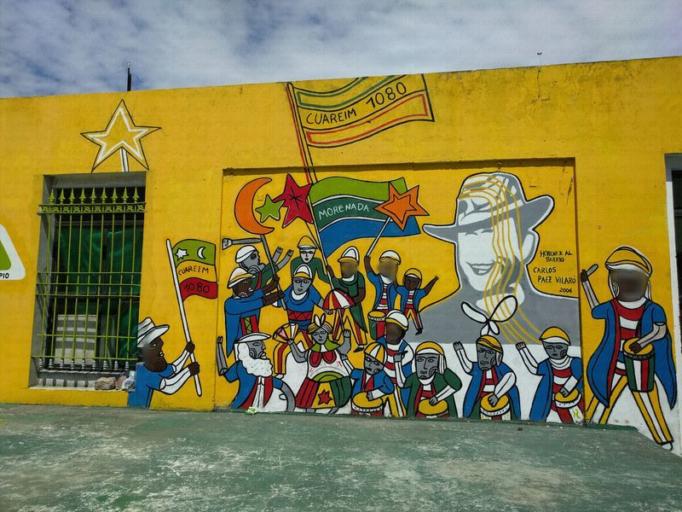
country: UY
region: Montevideo
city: Montevideo
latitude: -34.9115
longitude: -56.1898
